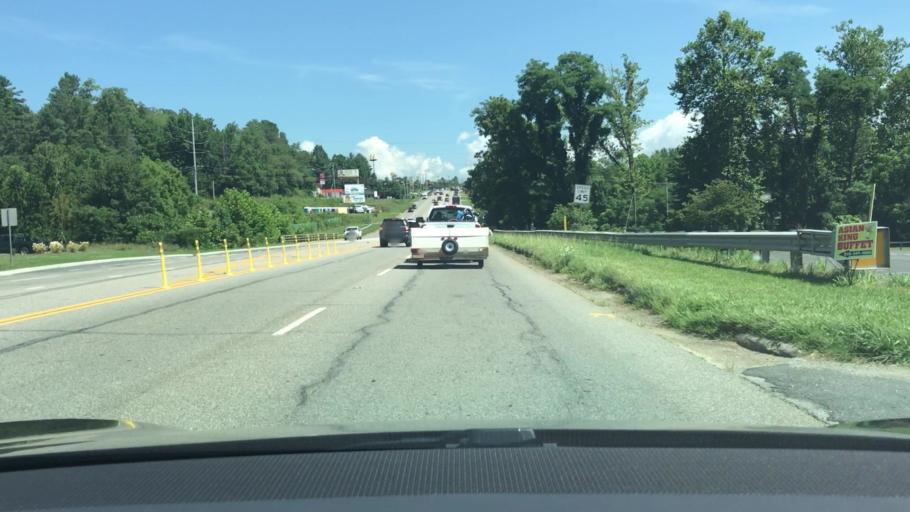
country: US
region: North Carolina
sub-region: Macon County
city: Franklin
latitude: 35.1574
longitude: -83.3916
